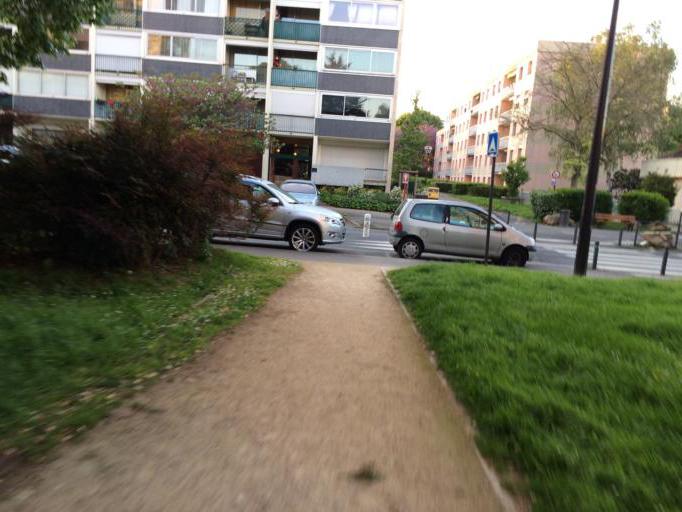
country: FR
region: Ile-de-France
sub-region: Departement de l'Essonne
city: Massy
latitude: 48.7281
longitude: 2.2849
